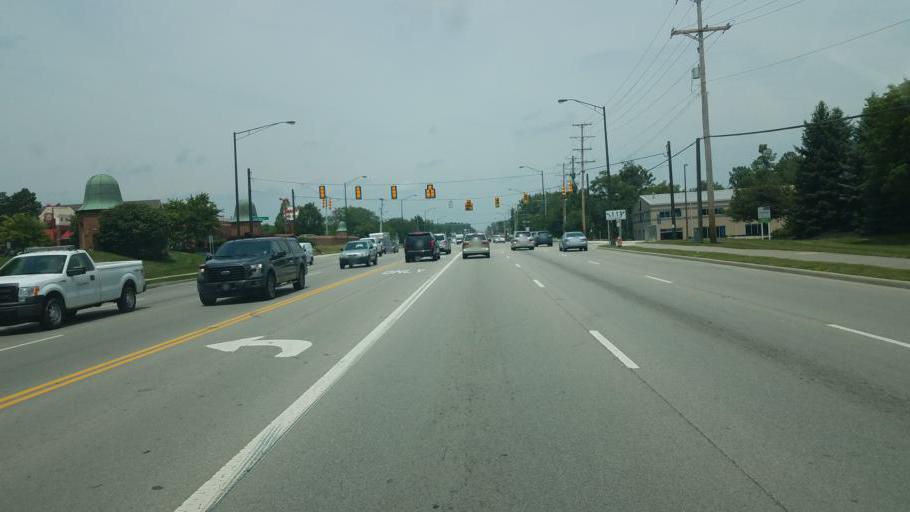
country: US
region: Ohio
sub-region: Franklin County
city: Worthington
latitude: 40.1293
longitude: -83.0164
